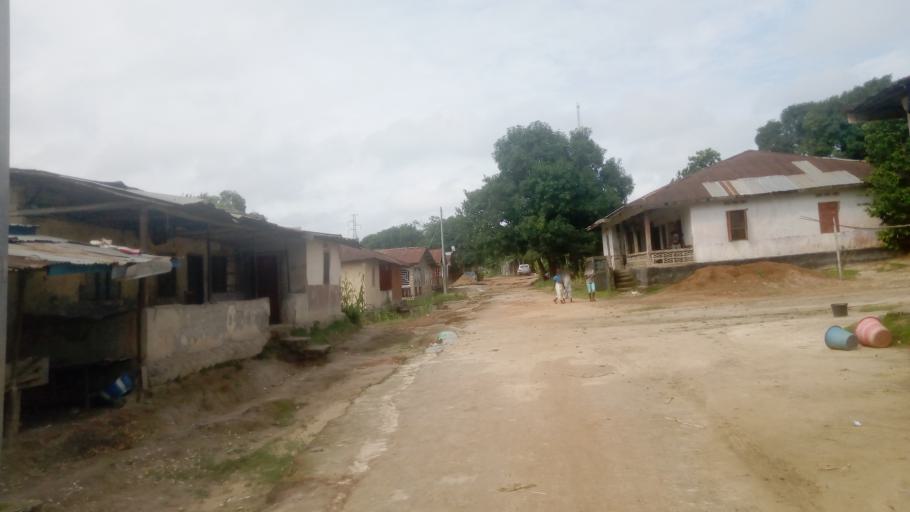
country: SL
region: Northern Province
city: Lunsar
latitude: 8.6928
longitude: -12.5356
